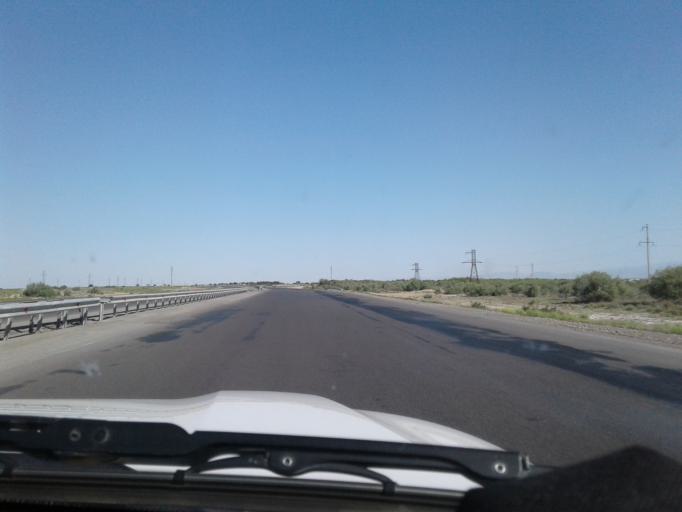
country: TM
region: Ahal
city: Kaka
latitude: 37.4862
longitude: 59.4735
